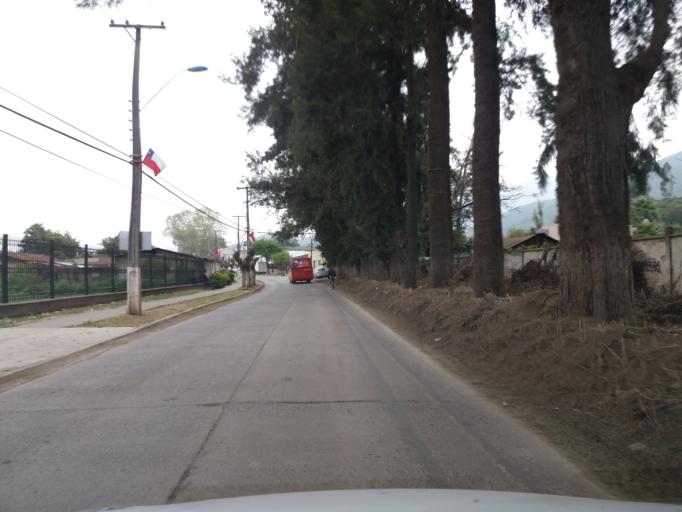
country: CL
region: Valparaiso
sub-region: Provincia de Quillota
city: Hacienda La Calera
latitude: -32.8040
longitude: -71.1432
